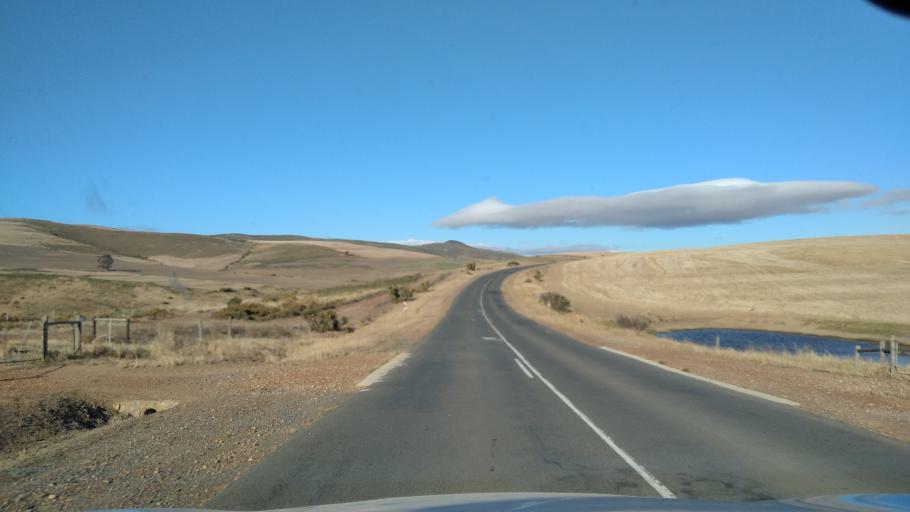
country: ZA
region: Western Cape
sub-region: Overberg District Municipality
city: Caledon
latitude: -34.1681
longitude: 19.2912
